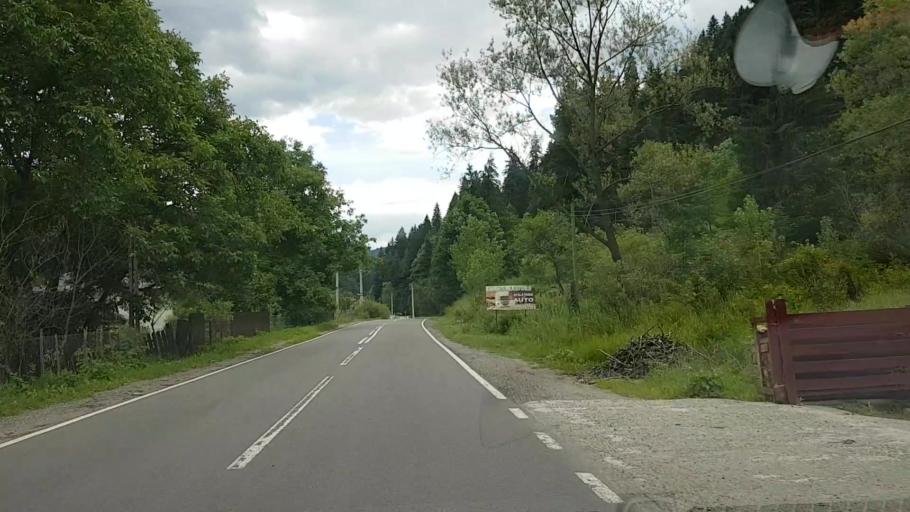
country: RO
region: Neamt
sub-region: Comuna Poiana Teiului
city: Poiana Teiului
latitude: 47.1063
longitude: 25.9338
